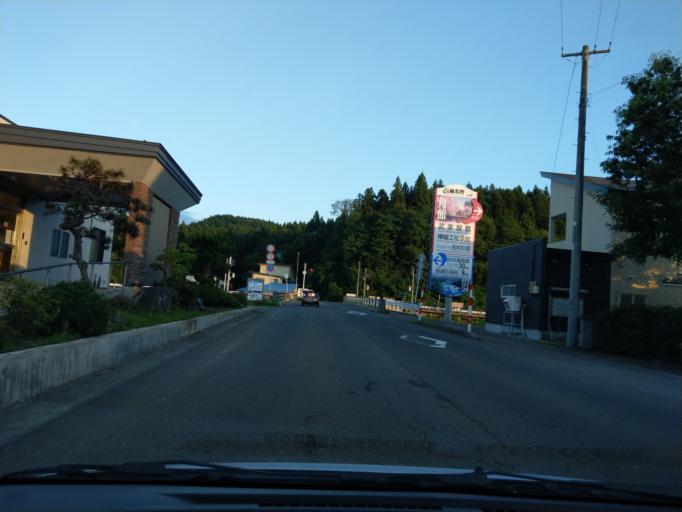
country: JP
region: Akita
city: Kakunodatemachi
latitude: 39.6104
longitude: 140.5701
